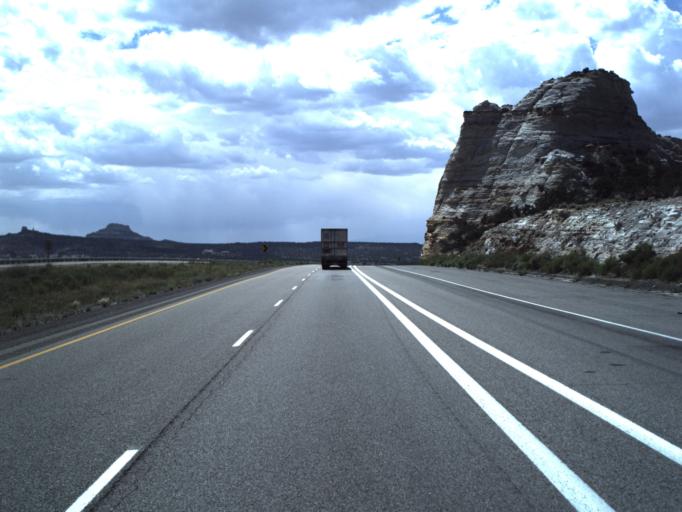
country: US
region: Utah
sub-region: Emery County
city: Ferron
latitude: 38.8620
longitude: -110.8148
